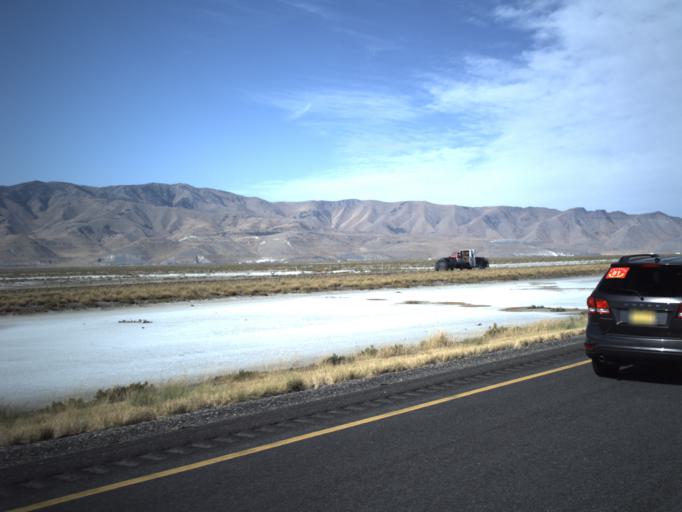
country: US
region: Utah
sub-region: Tooele County
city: Grantsville
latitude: 40.6971
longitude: -112.4778
